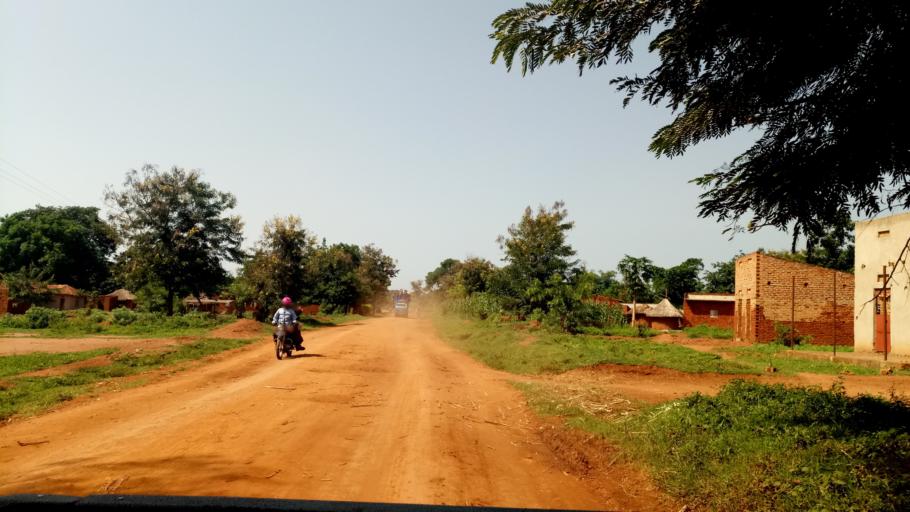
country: UG
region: Eastern Region
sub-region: Kaliro District
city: Kaliro
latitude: 0.9603
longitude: 33.4708
